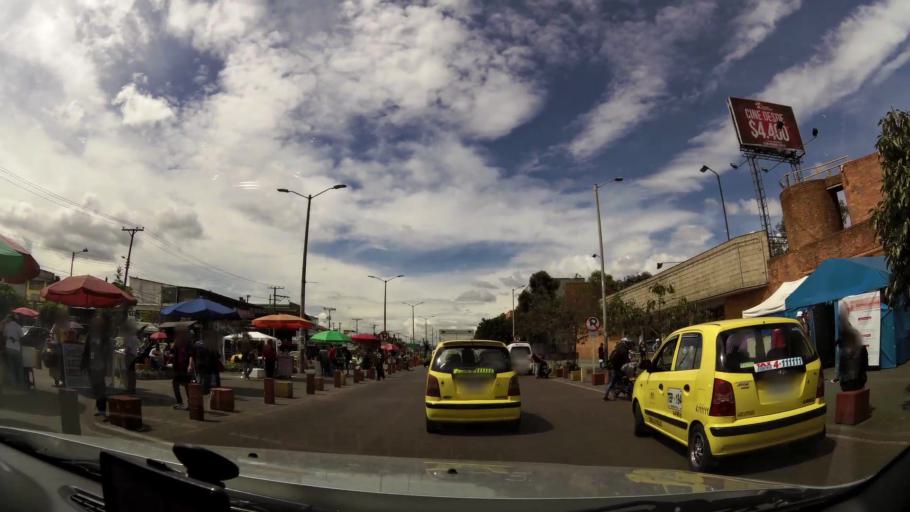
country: CO
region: Bogota D.C.
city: Bogota
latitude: 4.6181
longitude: -74.1374
